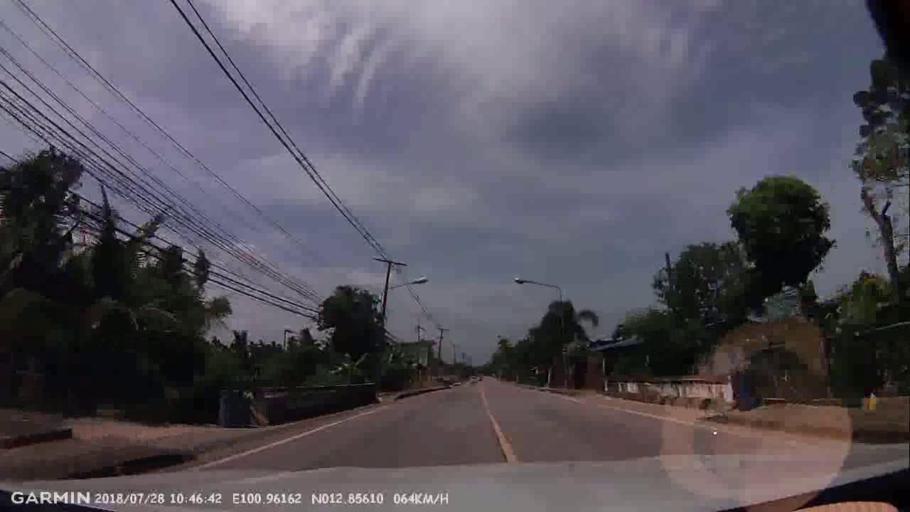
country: TH
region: Chon Buri
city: Phatthaya
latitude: 12.8559
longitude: 100.9616
